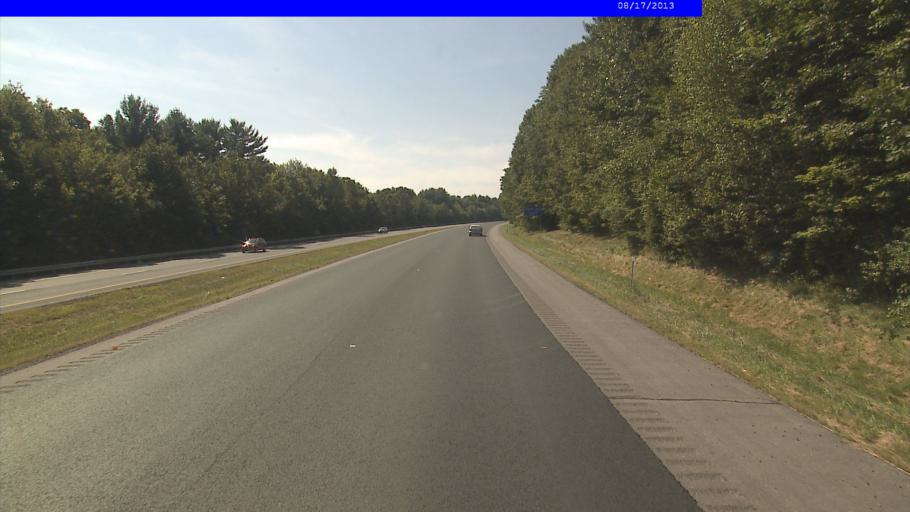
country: US
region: New Hampshire
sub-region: Cheshire County
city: Westmoreland
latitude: 43.0376
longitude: -72.4689
